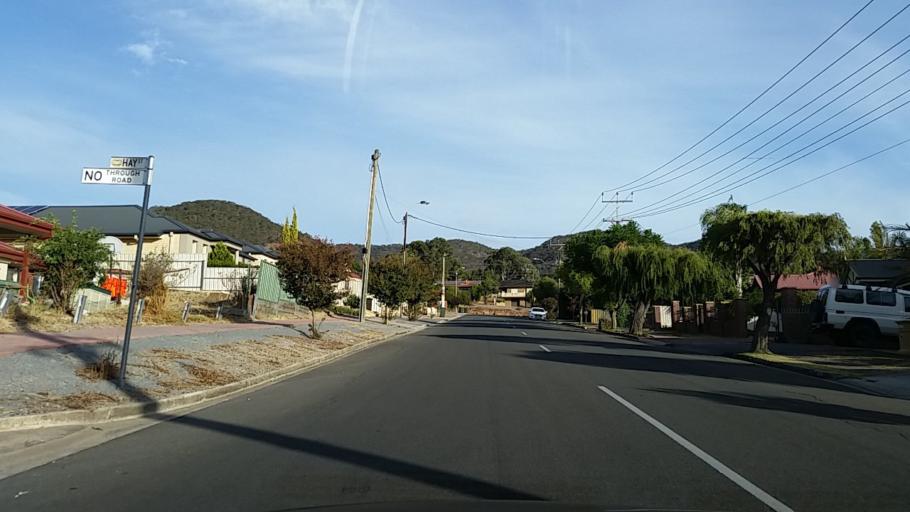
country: AU
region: South Australia
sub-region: Campbelltown
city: Athelstone
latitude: -34.8632
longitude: 138.7109
